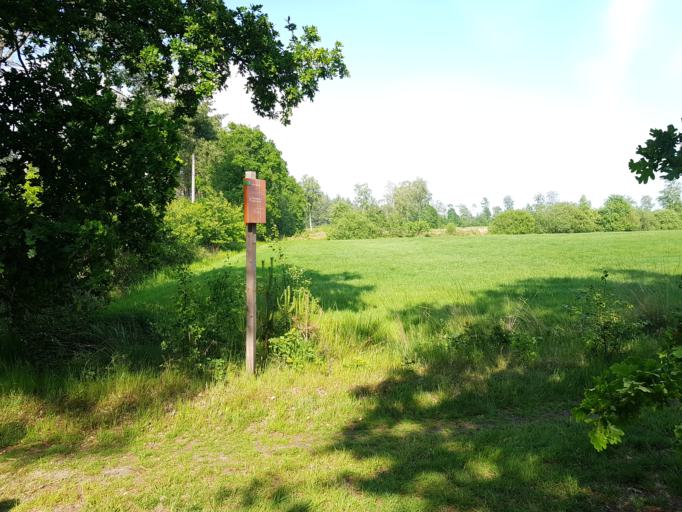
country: NL
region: Friesland
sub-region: Gemeente Heerenveen
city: Jubbega
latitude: 53.0448
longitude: 6.1200
